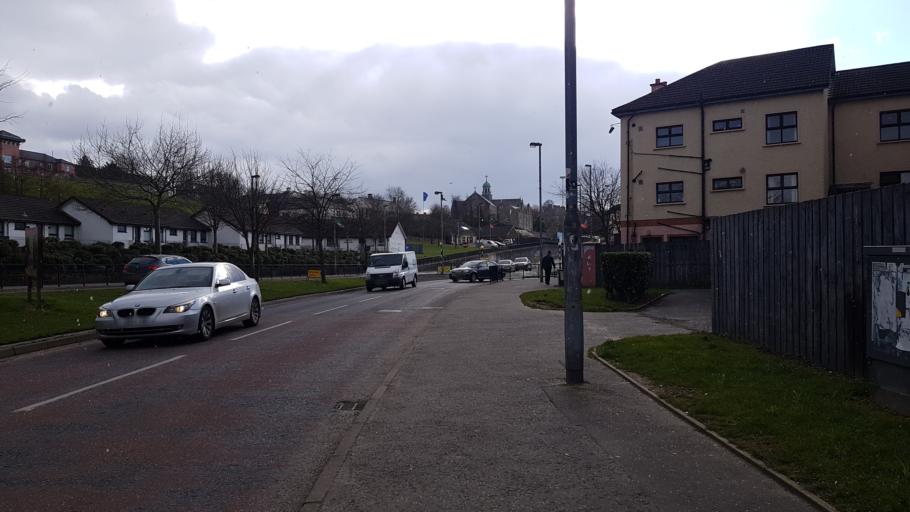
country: GB
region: Northern Ireland
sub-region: City of Derry
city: Derry
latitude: 54.9956
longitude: -7.3270
